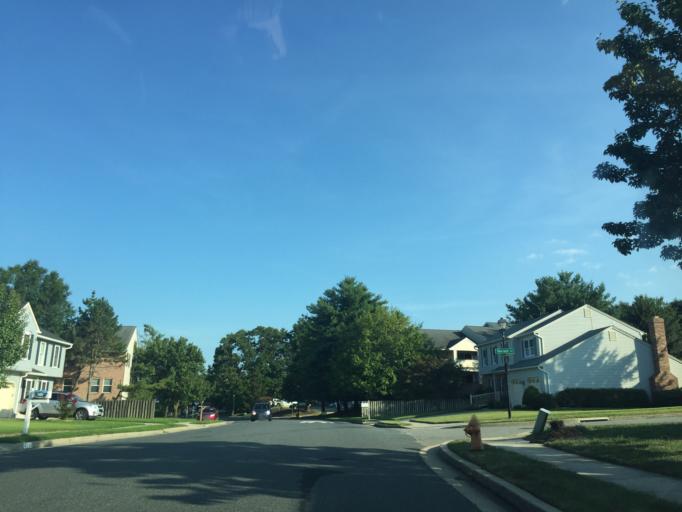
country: US
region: Maryland
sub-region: Baltimore County
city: Perry Hall
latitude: 39.3928
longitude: -76.4762
